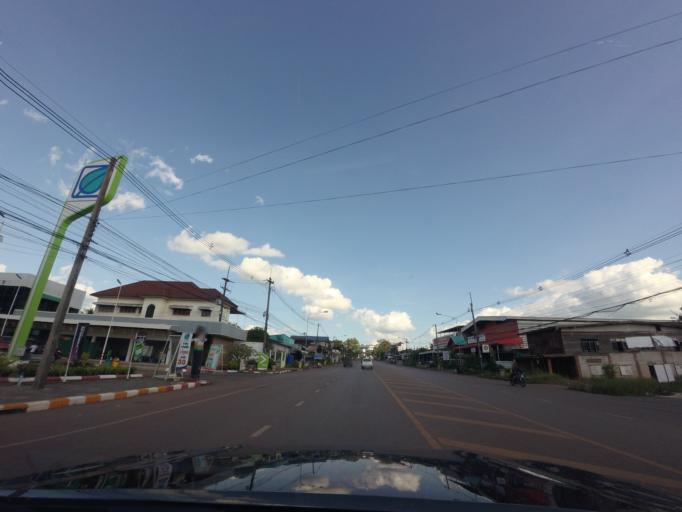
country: TH
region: Changwat Udon Thani
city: Ban Dung
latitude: 17.7029
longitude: 103.2557
